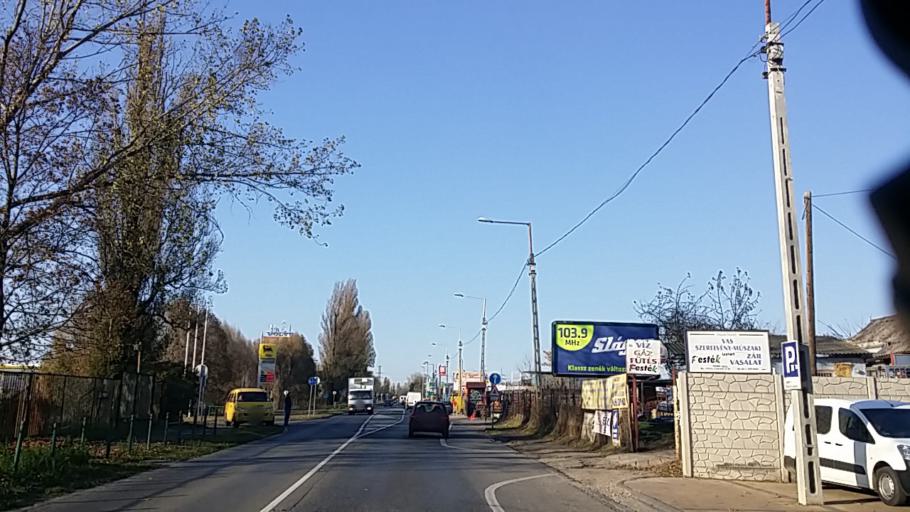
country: HU
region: Budapest
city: Budapest XVII. keruelet
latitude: 47.4922
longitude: 19.2425
